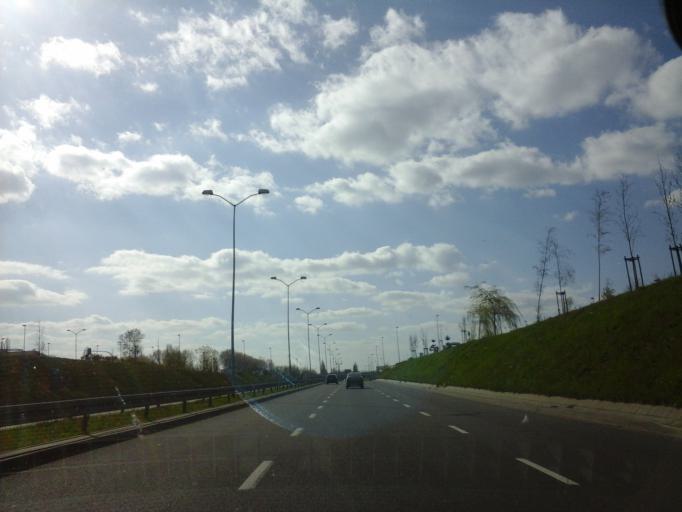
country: PL
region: West Pomeranian Voivodeship
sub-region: Szczecin
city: Szczecin
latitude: 53.3836
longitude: 14.6596
